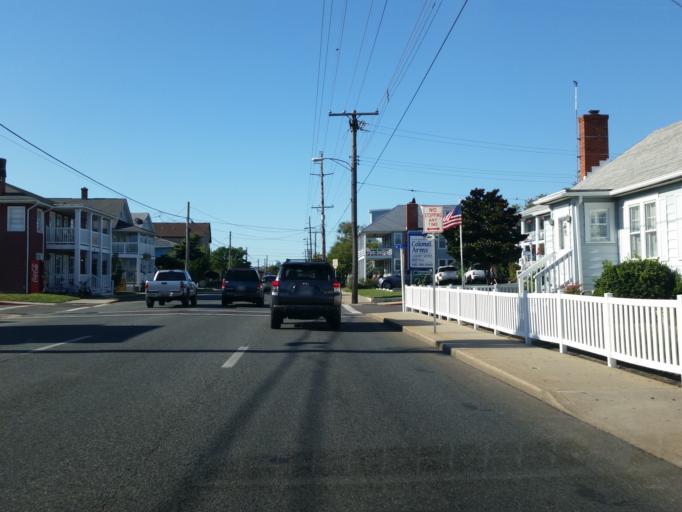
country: US
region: Maryland
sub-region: Worcester County
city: Ocean City
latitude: 38.3388
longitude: -75.0837
